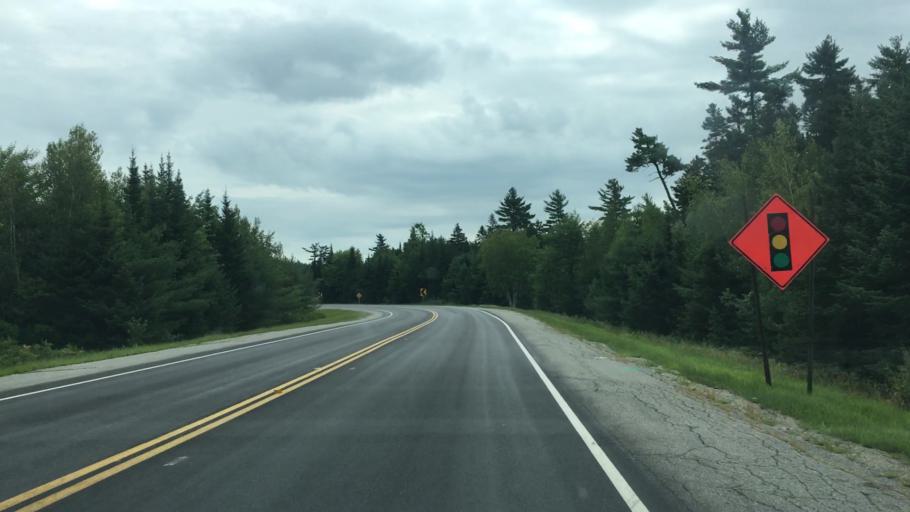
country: US
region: Maine
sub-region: Washington County
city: Addison
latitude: 44.9040
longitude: -67.8118
